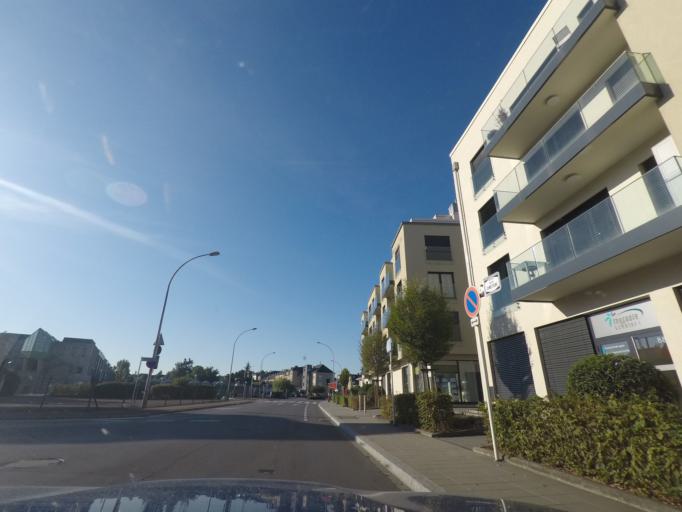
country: LU
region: Luxembourg
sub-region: Canton de Luxembourg
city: Luxembourg
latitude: 49.5919
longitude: 6.1415
